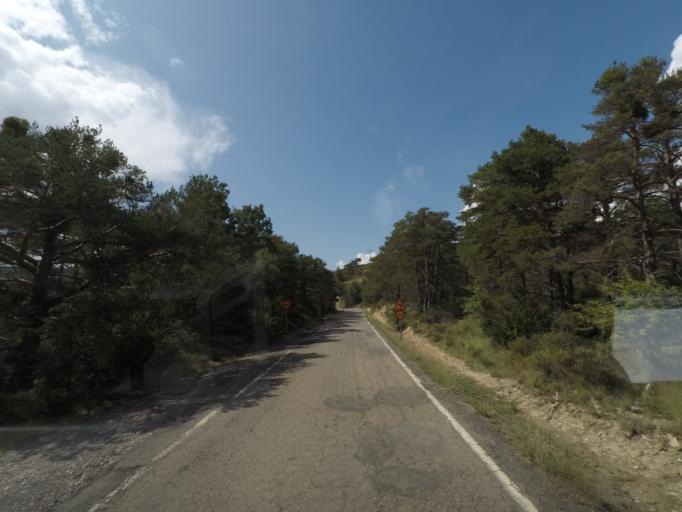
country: ES
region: Aragon
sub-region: Provincia de Huesca
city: Arguis
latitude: 42.4035
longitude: -0.3730
